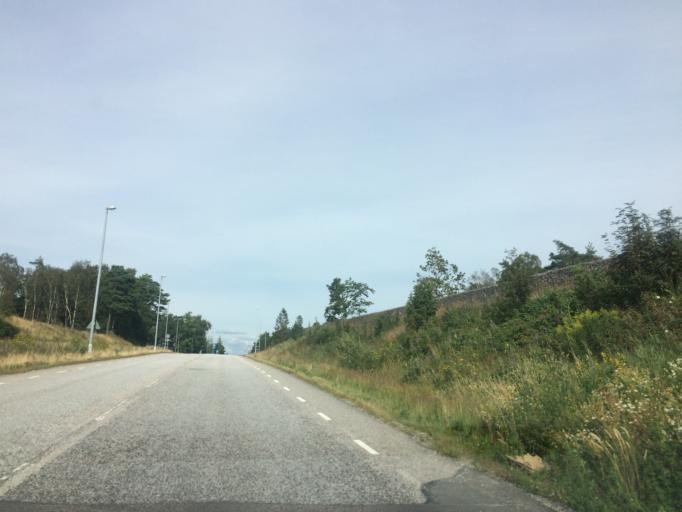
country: SE
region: Vaestra Goetaland
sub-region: Partille Kommun
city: Ojersjo
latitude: 57.6831
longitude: 12.0984
